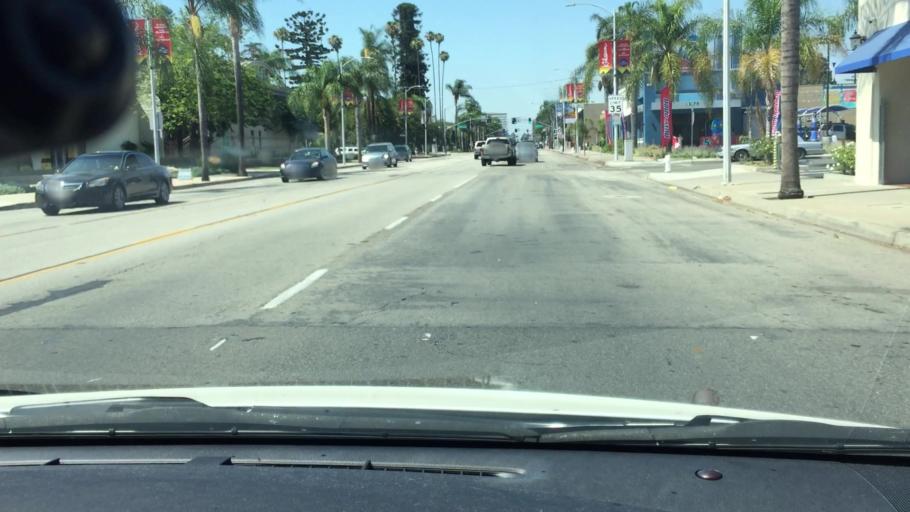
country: US
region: California
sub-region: Orange County
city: Santa Ana
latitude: 33.7608
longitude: -117.8675
